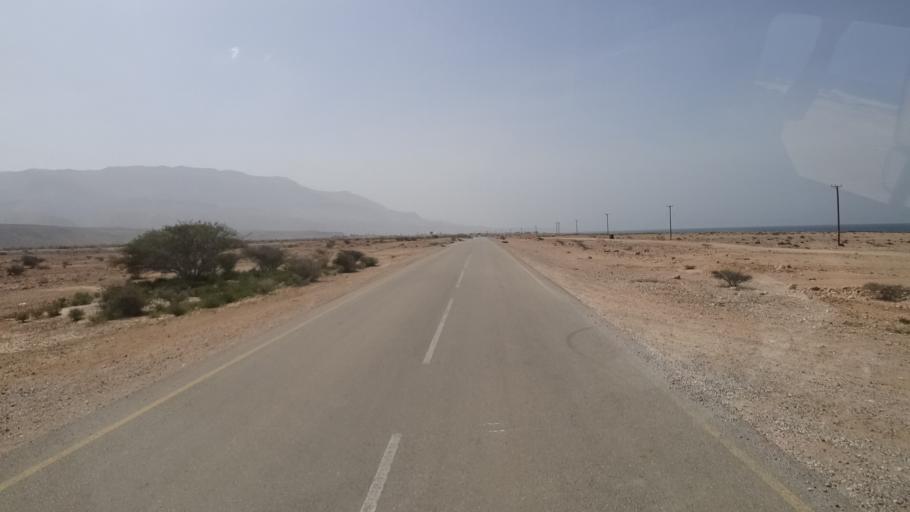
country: OM
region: Ash Sharqiyah
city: Sur
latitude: 22.9794
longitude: 59.1549
